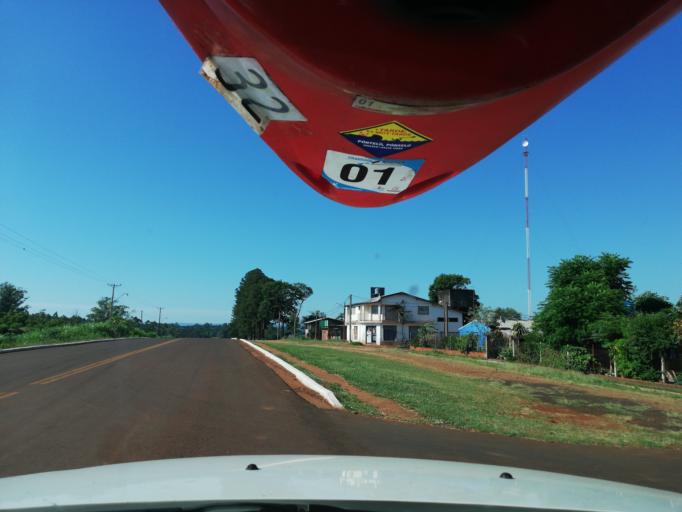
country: AR
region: Misiones
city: Puerto Leoni
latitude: -26.9891
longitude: -55.1646
